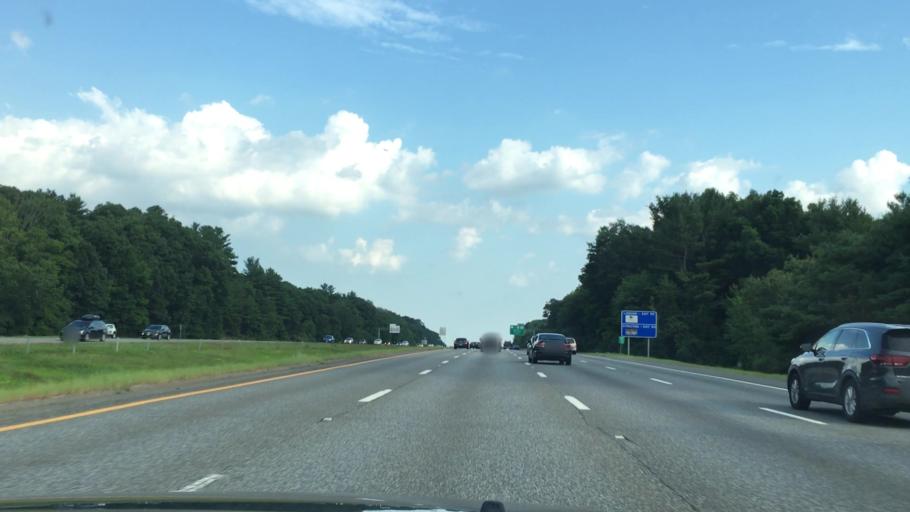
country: US
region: Massachusetts
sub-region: Essex County
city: Topsfield
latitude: 42.6149
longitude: -70.9762
